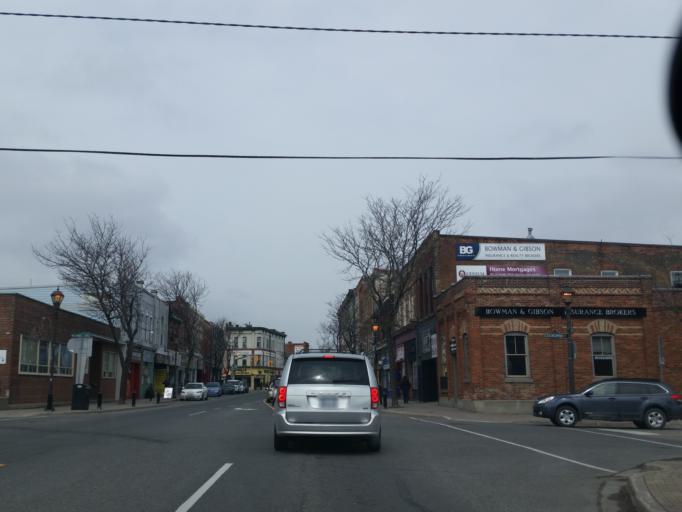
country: CA
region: Ontario
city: Oshawa
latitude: 43.8786
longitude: -78.9417
